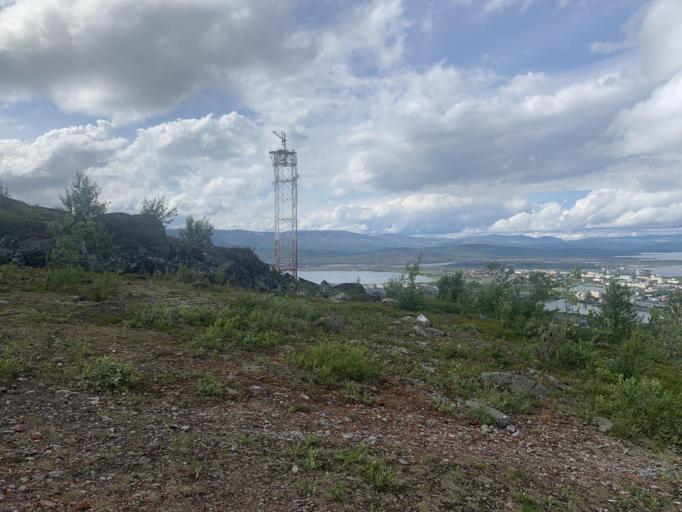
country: RU
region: Murmansk
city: Monchegorsk
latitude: 67.9167
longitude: 32.9785
